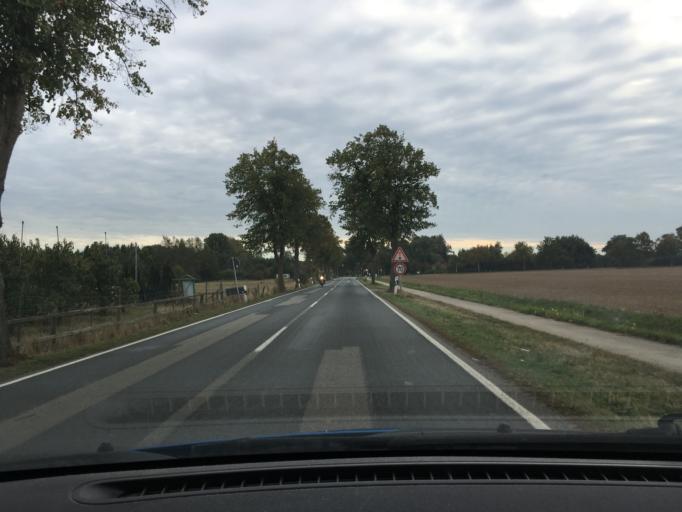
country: DE
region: Lower Saxony
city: Drage
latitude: 53.3871
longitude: 10.2449
